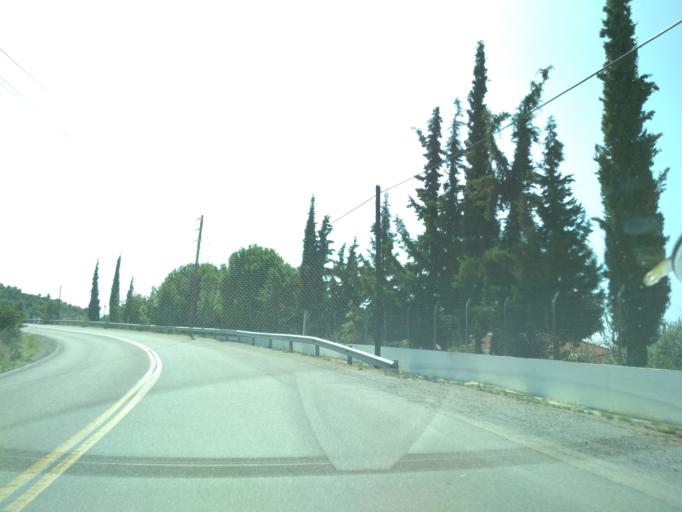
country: GR
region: Central Greece
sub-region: Nomos Evvoias
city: Roviai
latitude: 38.8418
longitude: 23.1714
